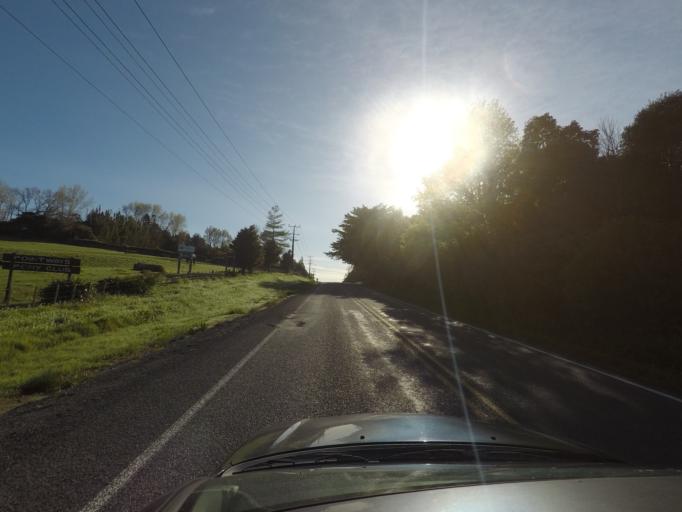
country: NZ
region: Auckland
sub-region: Auckland
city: Red Hill
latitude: -37.0139
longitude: 174.9469
